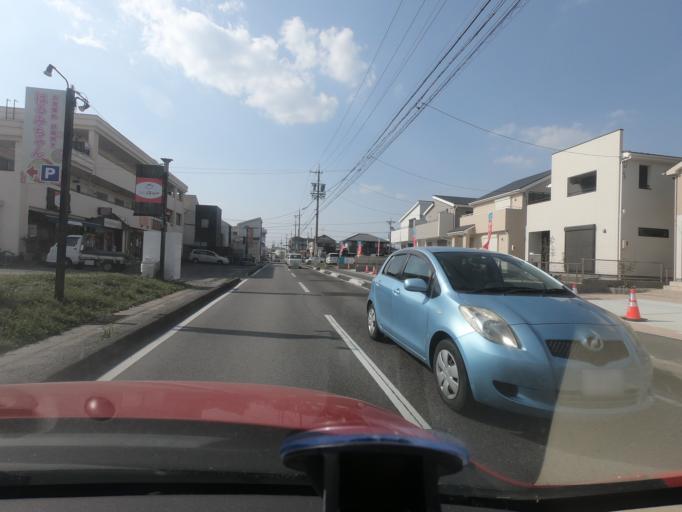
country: JP
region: Aichi
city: Kasugai
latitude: 35.2493
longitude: 136.9683
